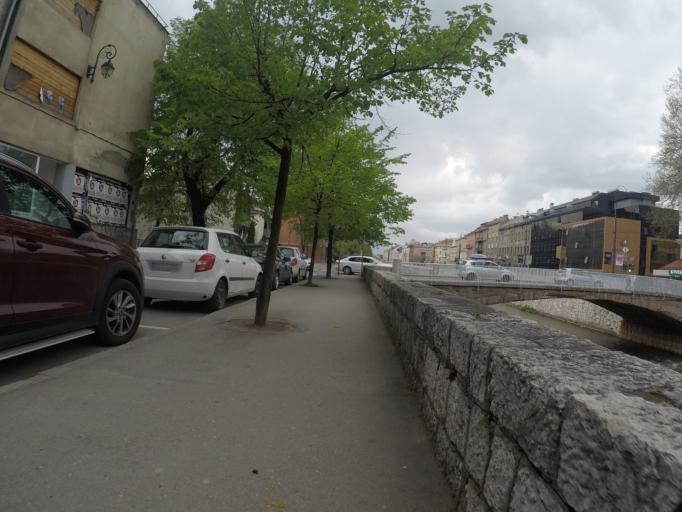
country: BA
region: Federation of Bosnia and Herzegovina
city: Kobilja Glava
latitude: 43.8580
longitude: 18.4312
